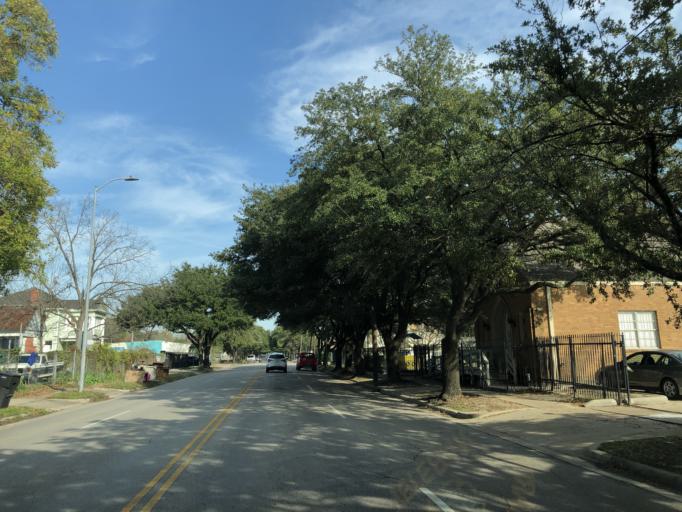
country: US
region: Texas
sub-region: Harris County
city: Houston
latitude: 29.7934
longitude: -95.3990
